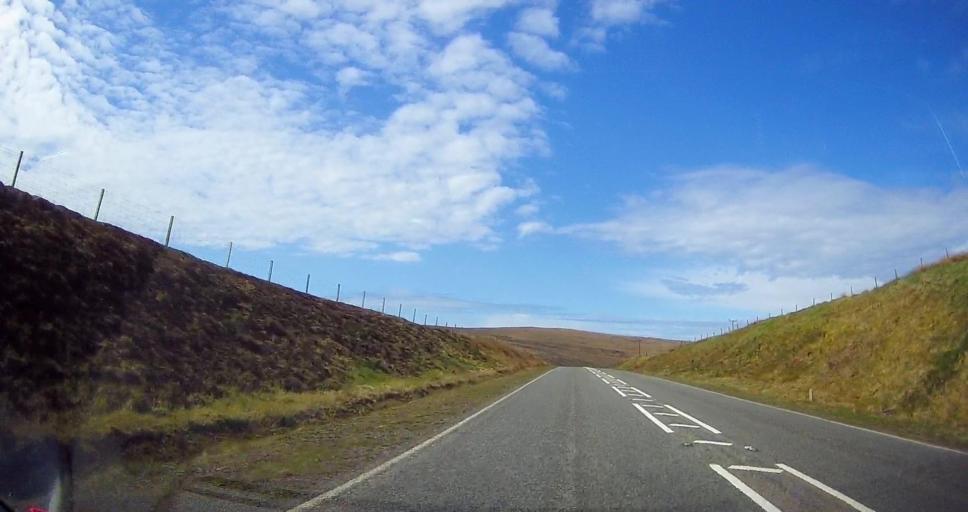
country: GB
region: Scotland
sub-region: Shetland Islands
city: Sandwick
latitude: 60.0096
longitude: -1.2657
